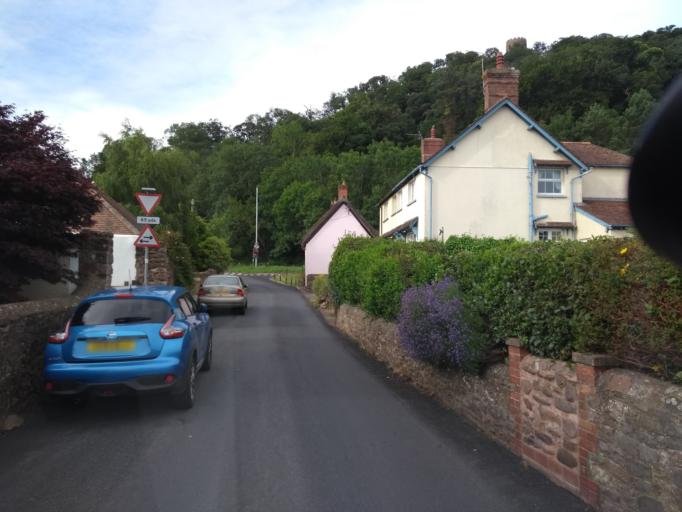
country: GB
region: England
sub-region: Somerset
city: Minehead
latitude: 51.1889
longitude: -3.4417
